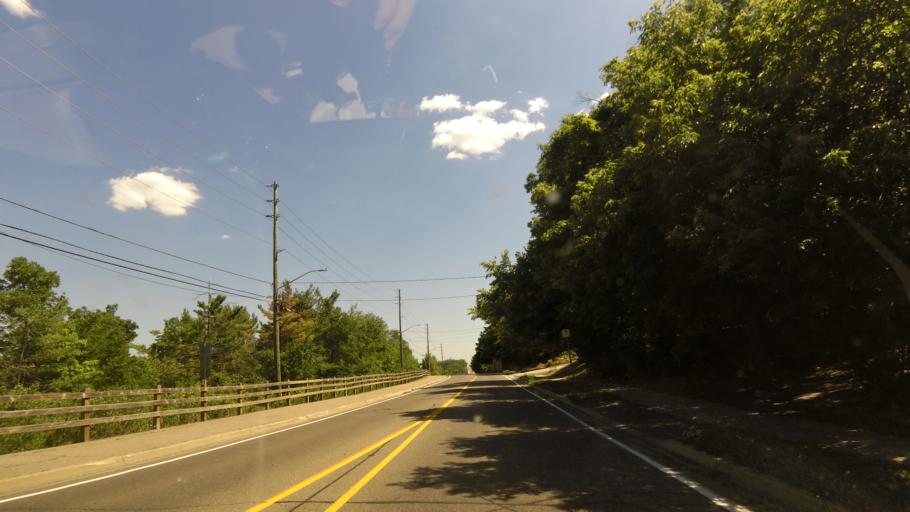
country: CA
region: Ontario
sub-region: Halton
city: Milton
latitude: 43.6448
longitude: -79.9200
